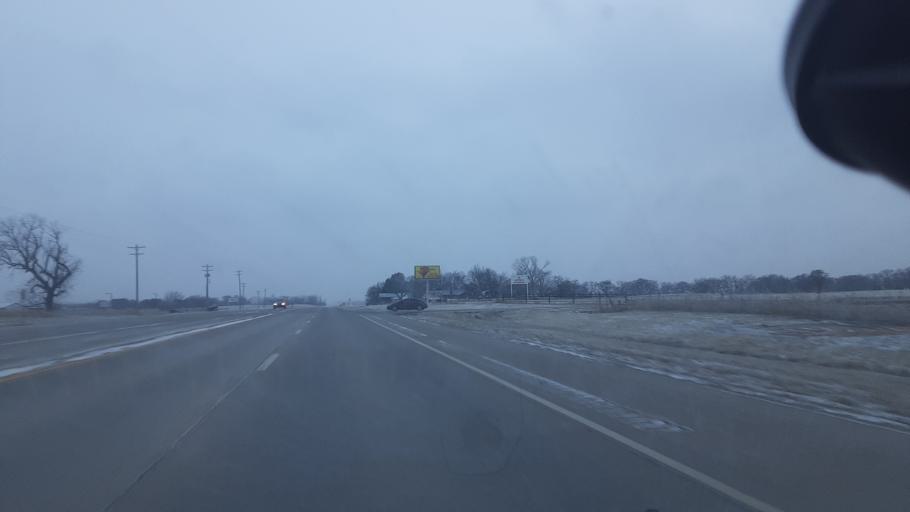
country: US
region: Oklahoma
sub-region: Payne County
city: Perkins
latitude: 35.9854
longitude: -97.0864
